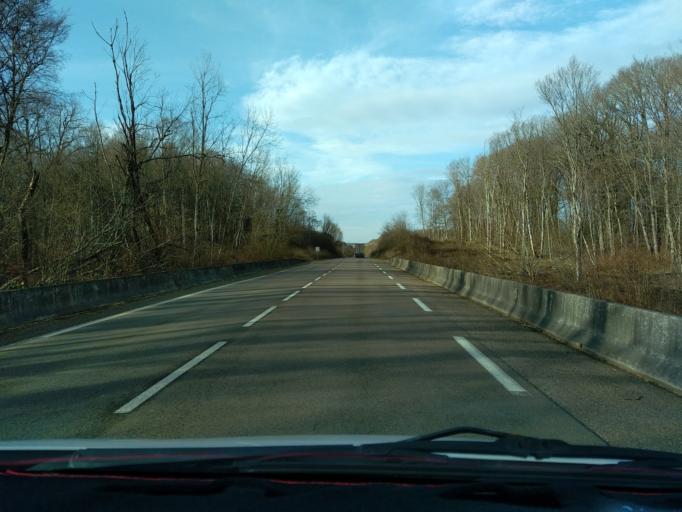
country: FR
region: Franche-Comte
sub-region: Departement de la Haute-Saone
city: Gray
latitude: 47.4096
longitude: 5.6325
